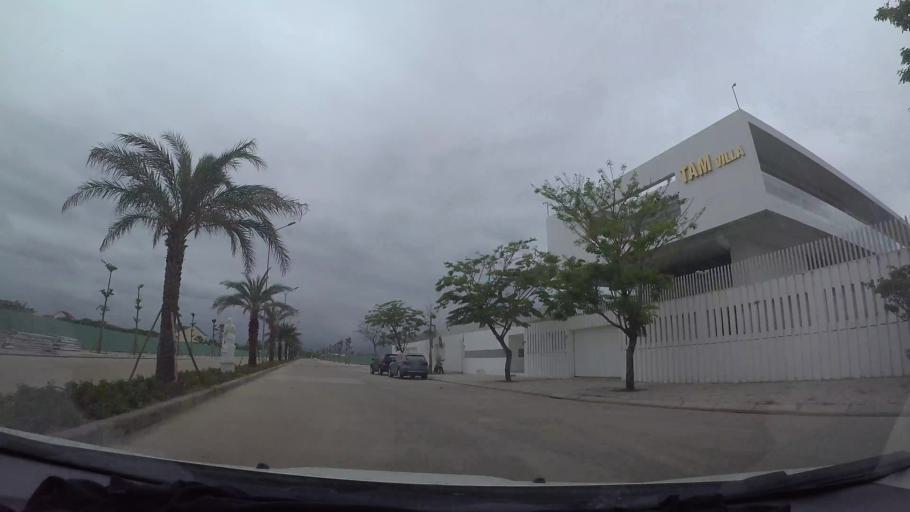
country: VN
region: Da Nang
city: Lien Chieu
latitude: 16.1071
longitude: 108.1198
